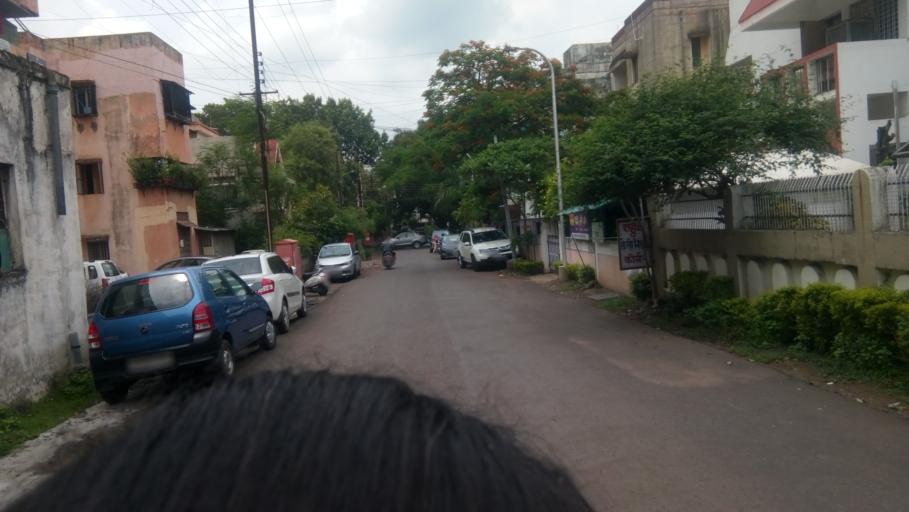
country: IN
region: Maharashtra
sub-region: Nagpur Division
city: Nagpur
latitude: 21.1077
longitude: 79.0644
